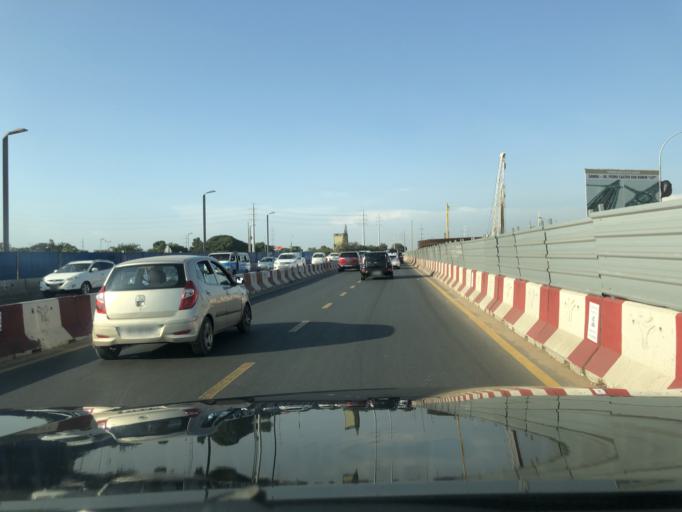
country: AO
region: Luanda
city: Luanda
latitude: -8.9096
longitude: 13.1791
